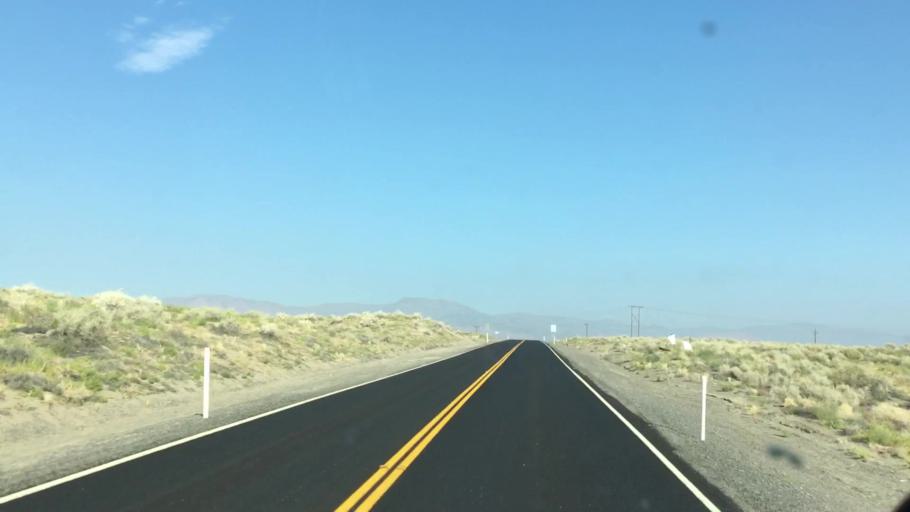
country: US
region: Nevada
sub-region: Lyon County
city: Fernley
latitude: 39.6397
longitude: -119.2953
